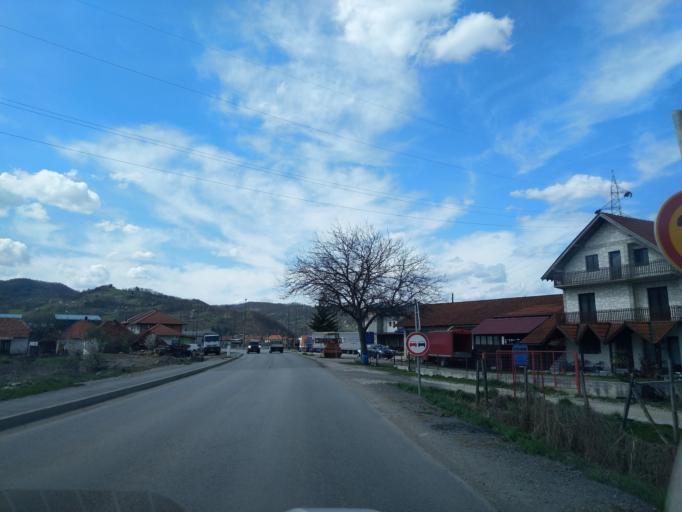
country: RS
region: Central Serbia
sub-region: Zlatiborski Okrug
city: Arilje
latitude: 43.7554
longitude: 20.1026
